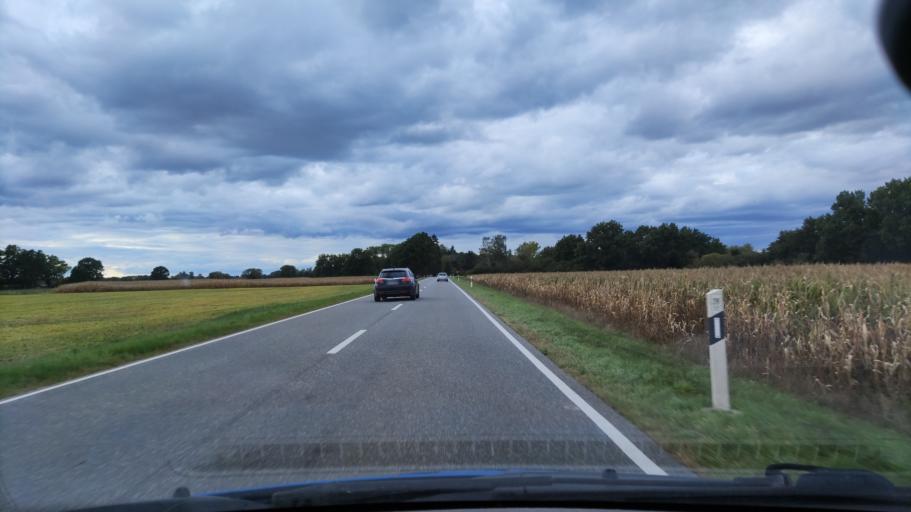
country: DE
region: Lower Saxony
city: Neu Darchau
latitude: 53.3078
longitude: 10.9619
